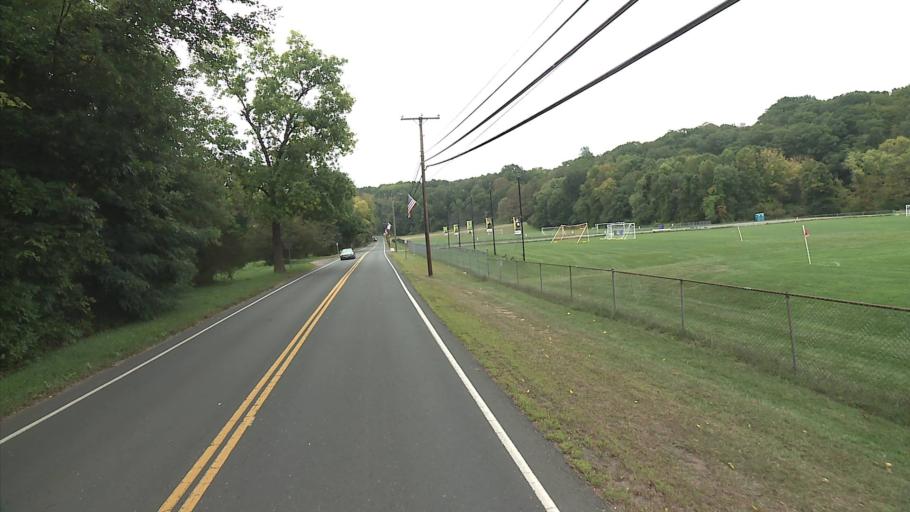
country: US
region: Connecticut
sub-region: Hartford County
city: Tariffville
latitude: 41.8970
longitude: -72.7776
